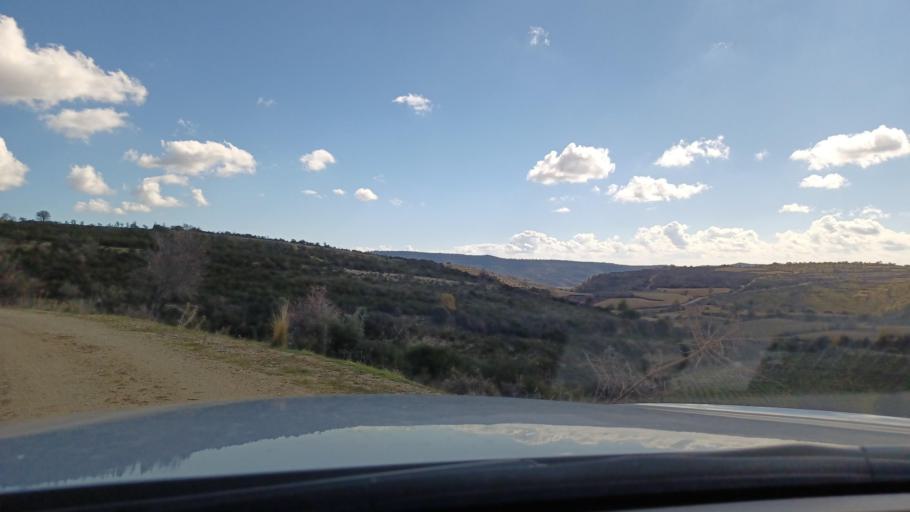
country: CY
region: Limassol
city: Pachna
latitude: 34.8195
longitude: 32.7674
